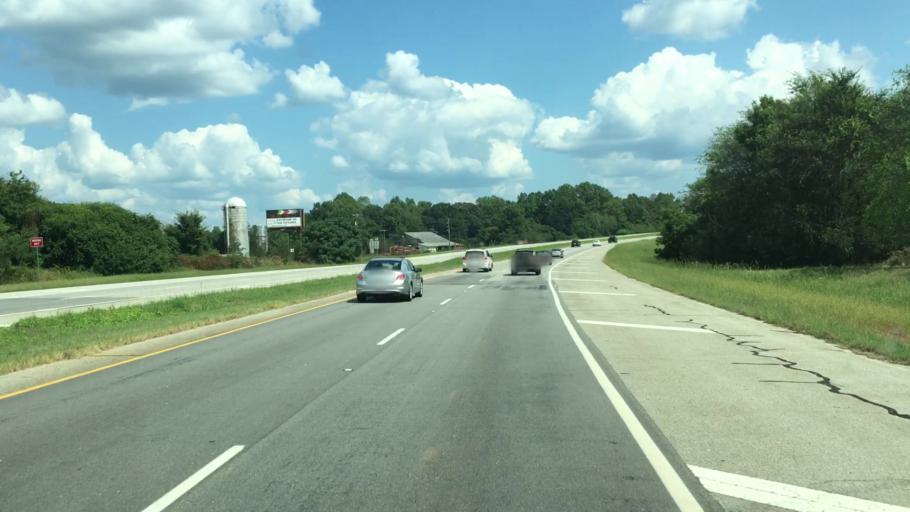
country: US
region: Georgia
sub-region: Putnam County
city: Eatonton
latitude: 33.2965
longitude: -83.3823
